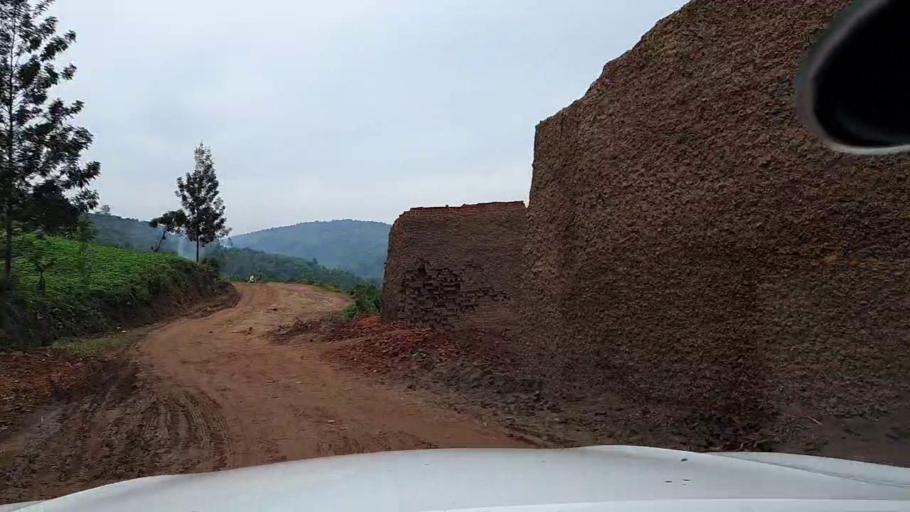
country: RW
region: Kigali
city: Kigali
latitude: -1.9540
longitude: 29.9933
